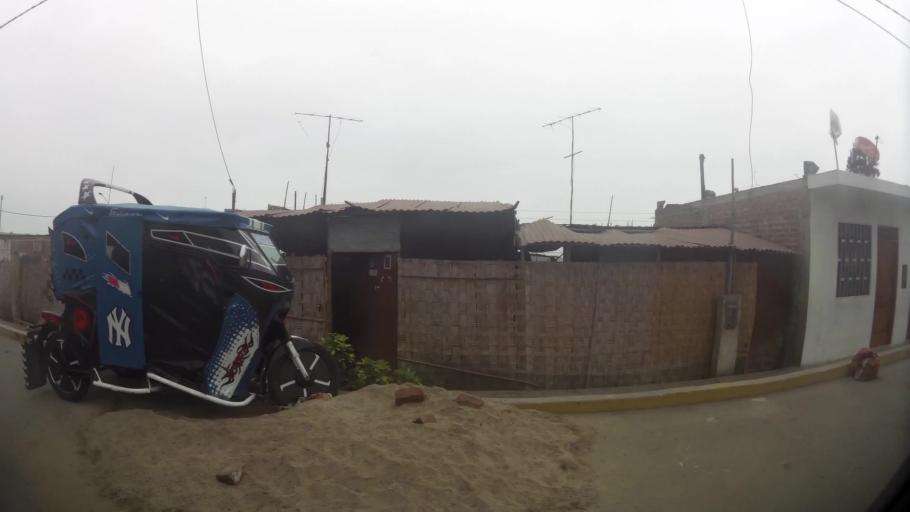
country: PE
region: Lima
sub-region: Provincia de Huaral
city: Chancay
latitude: -11.5950
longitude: -77.2547
